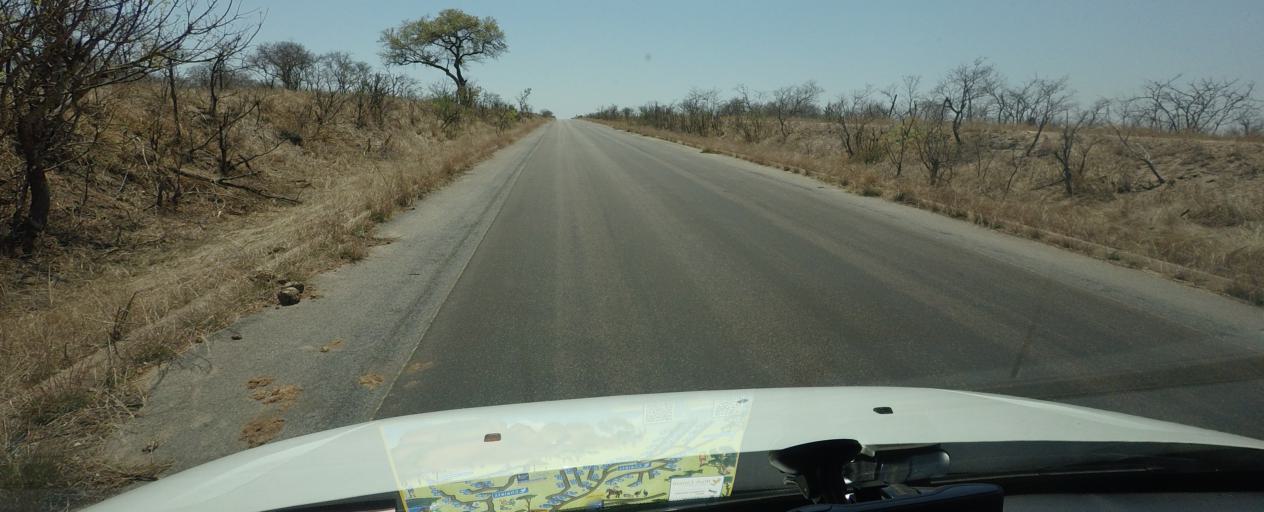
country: ZA
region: Limpopo
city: Thulamahashi
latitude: -24.5192
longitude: 31.3787
